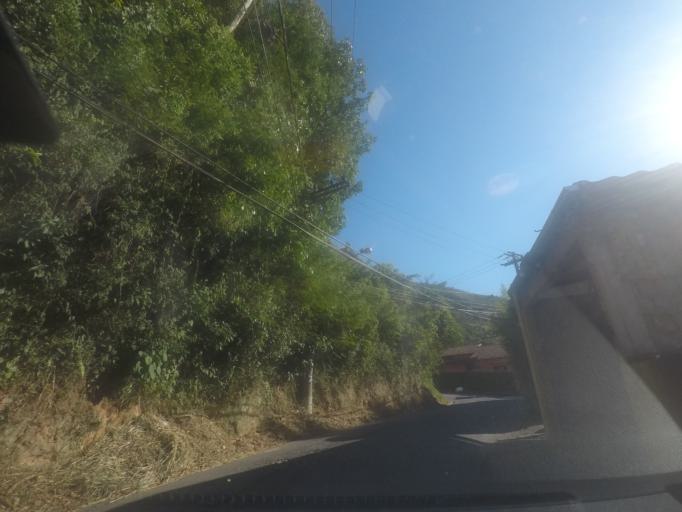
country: BR
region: Rio de Janeiro
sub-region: Petropolis
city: Petropolis
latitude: -22.5061
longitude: -43.1575
